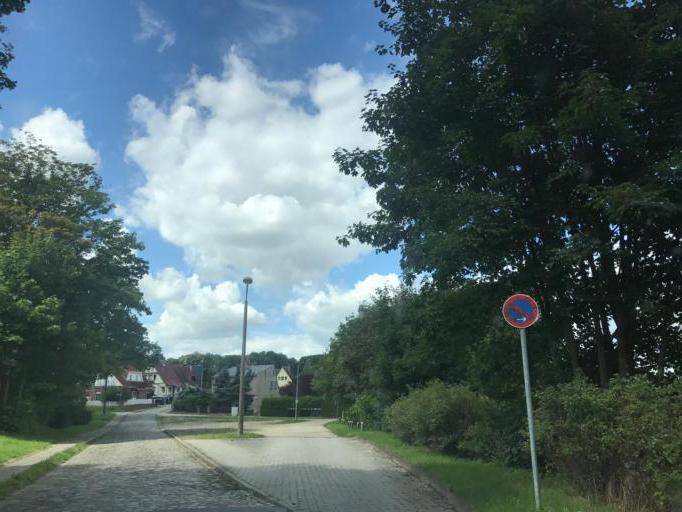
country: DE
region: Brandenburg
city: Gransee
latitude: 53.0053
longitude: 13.1462
